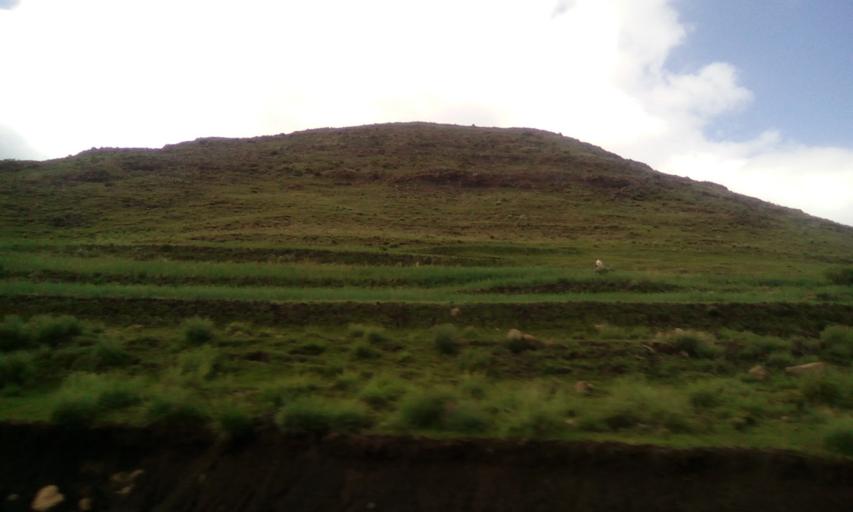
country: LS
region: Maseru
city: Nako
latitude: -29.6575
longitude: 27.8702
